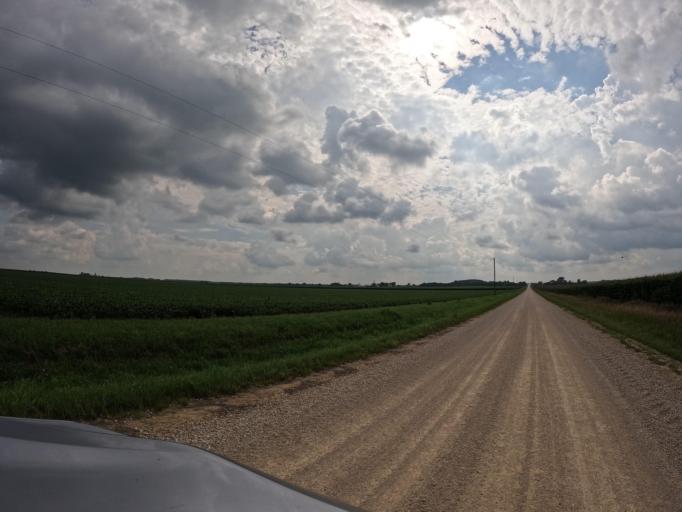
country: US
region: Iowa
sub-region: Clinton County
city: De Witt
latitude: 41.8013
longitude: -90.4002
